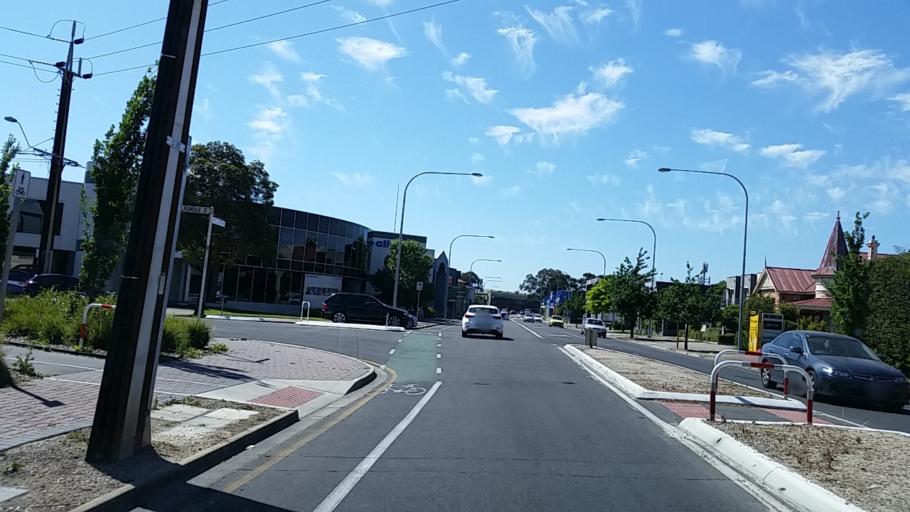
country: AU
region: South Australia
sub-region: Norwood Payneham St Peters
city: Trinity Gardens
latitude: -34.9186
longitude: 138.6229
